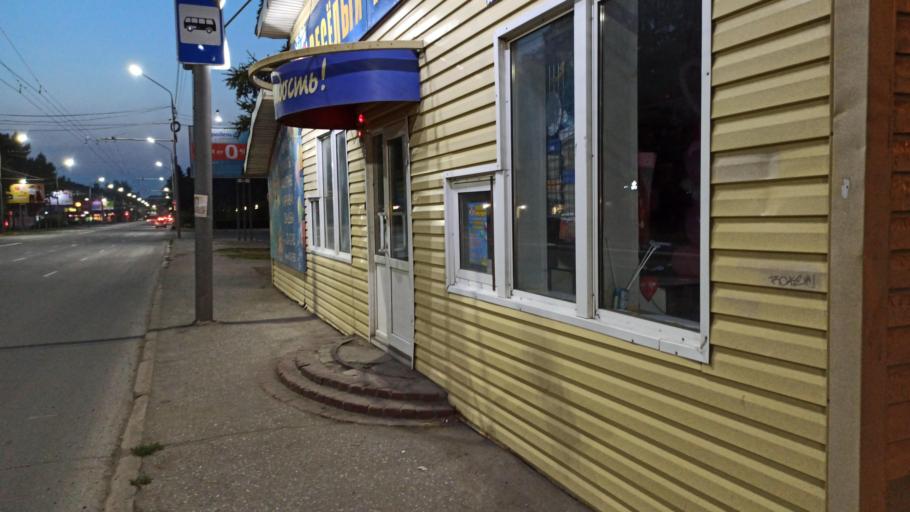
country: RU
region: Tomsk
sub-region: Tomskiy Rayon
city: Tomsk
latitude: 56.4595
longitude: 84.9706
